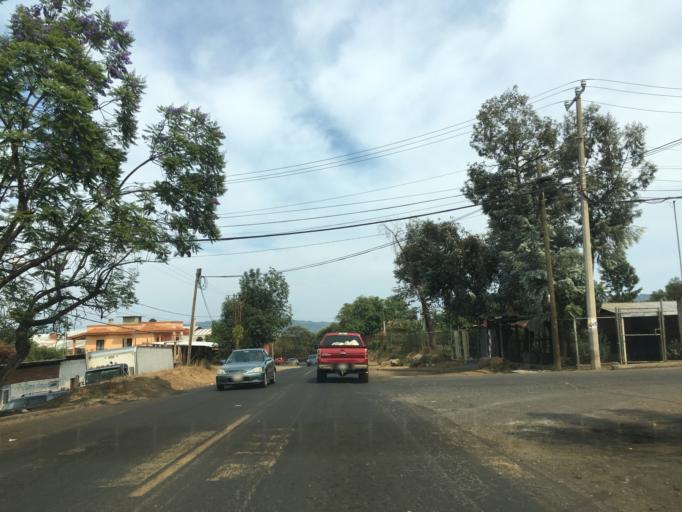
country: MX
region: Michoacan
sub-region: Uruapan
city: Uruapan
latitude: 19.3812
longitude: -102.0795
